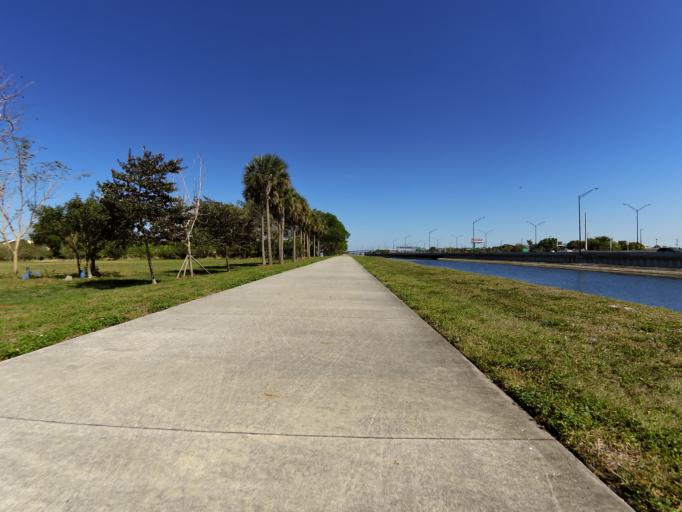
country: US
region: Florida
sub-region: Broward County
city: Pine Island Ridge
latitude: 26.1028
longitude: -80.2615
